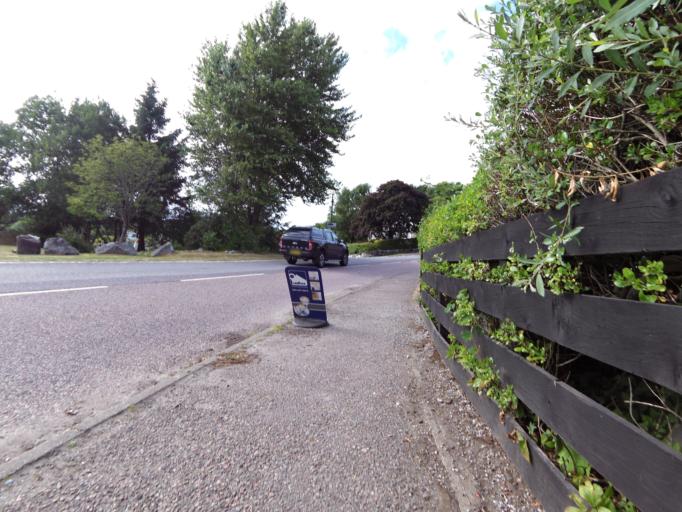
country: GB
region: Scotland
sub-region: Argyll and Bute
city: Isle Of Mull
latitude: 56.9106
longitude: -5.8483
